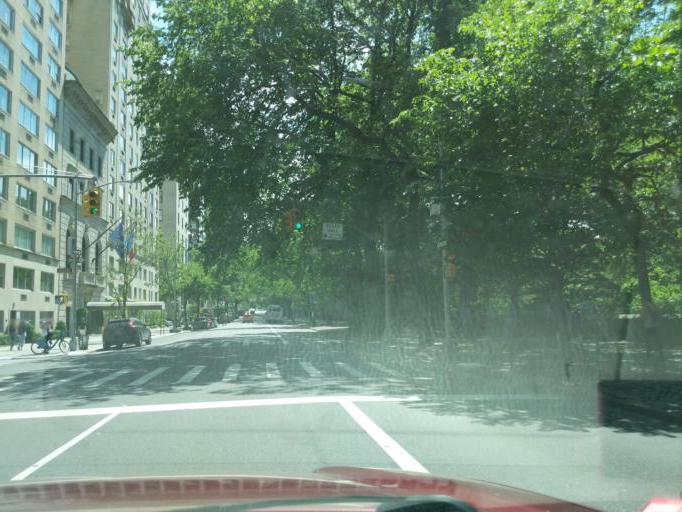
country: US
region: New York
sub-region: New York County
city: Manhattan
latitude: 40.7746
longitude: -73.9655
